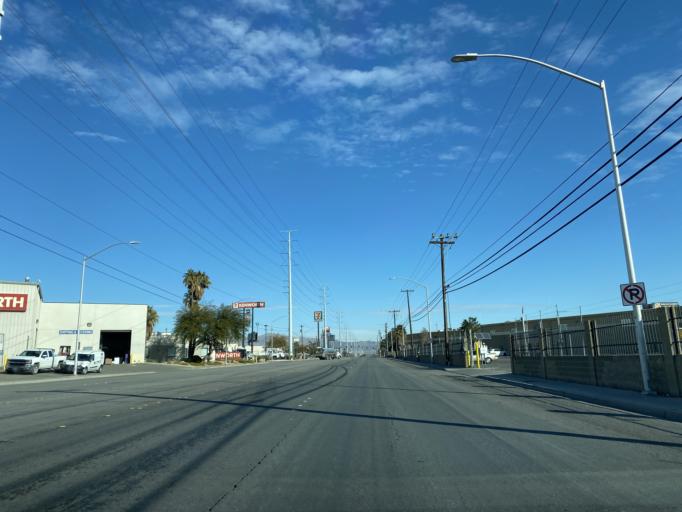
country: US
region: Nevada
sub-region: Clark County
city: North Las Vegas
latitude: 36.2146
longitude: -115.1294
